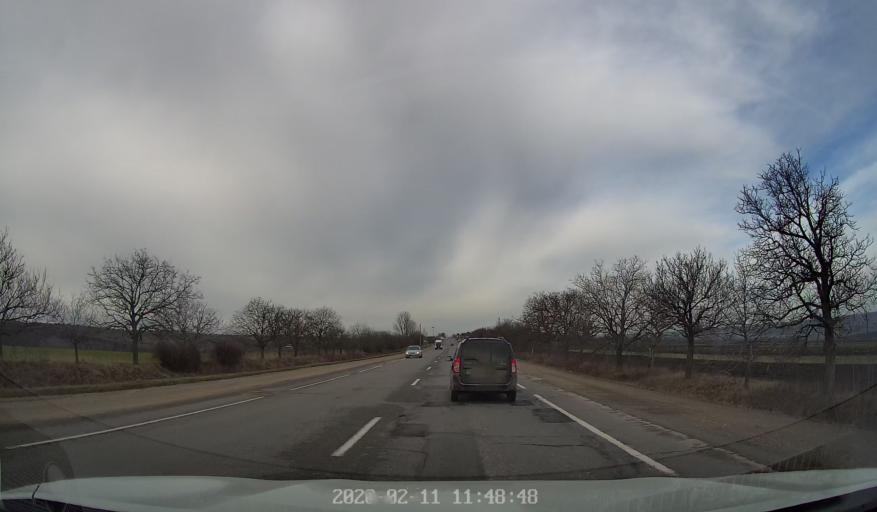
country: MD
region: Balti
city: Balti
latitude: 47.8422
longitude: 27.7990
